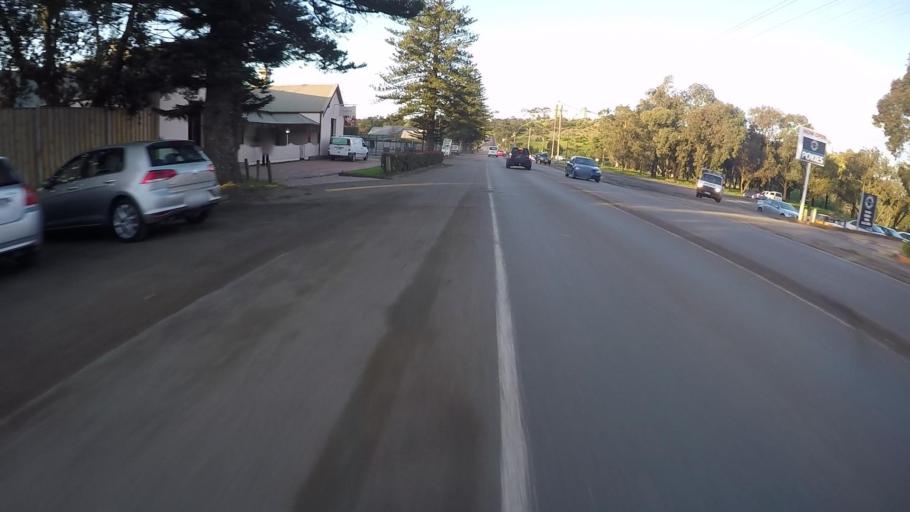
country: AU
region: Victoria
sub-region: Greater Geelong
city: Hamlyn Heights
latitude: -38.1418
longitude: 144.3096
